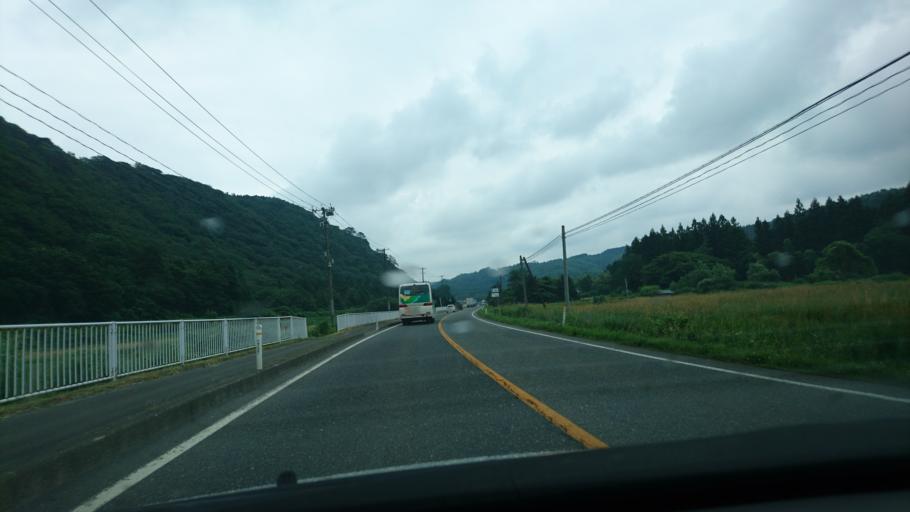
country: JP
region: Miyagi
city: Furukawa
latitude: 38.7237
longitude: 140.8002
